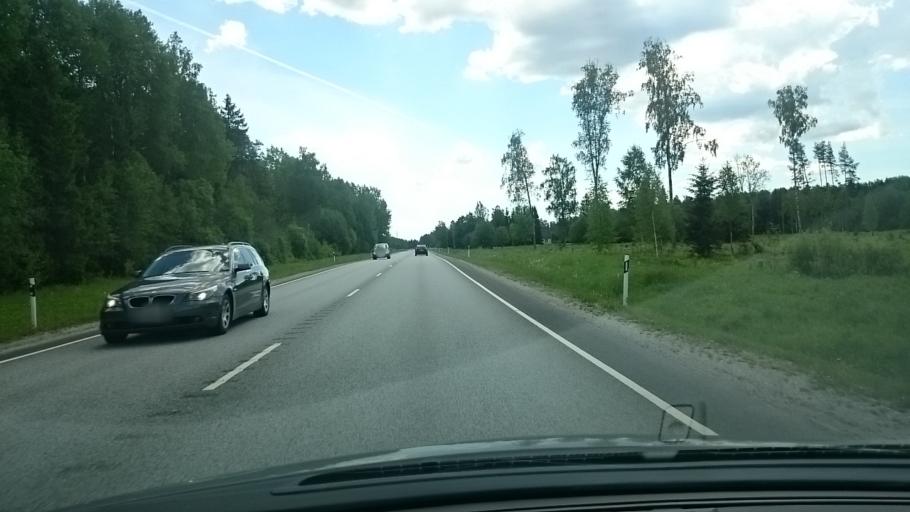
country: EE
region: Jaervamaa
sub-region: Paide linn
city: Paide
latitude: 59.0454
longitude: 25.4385
